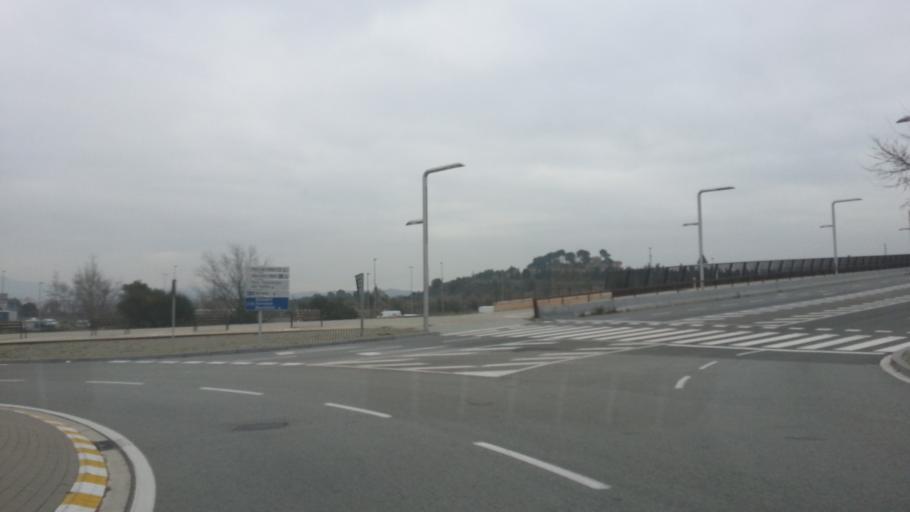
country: ES
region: Catalonia
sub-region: Provincia de Barcelona
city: Barbera del Valles
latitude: 41.4962
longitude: 2.1092
